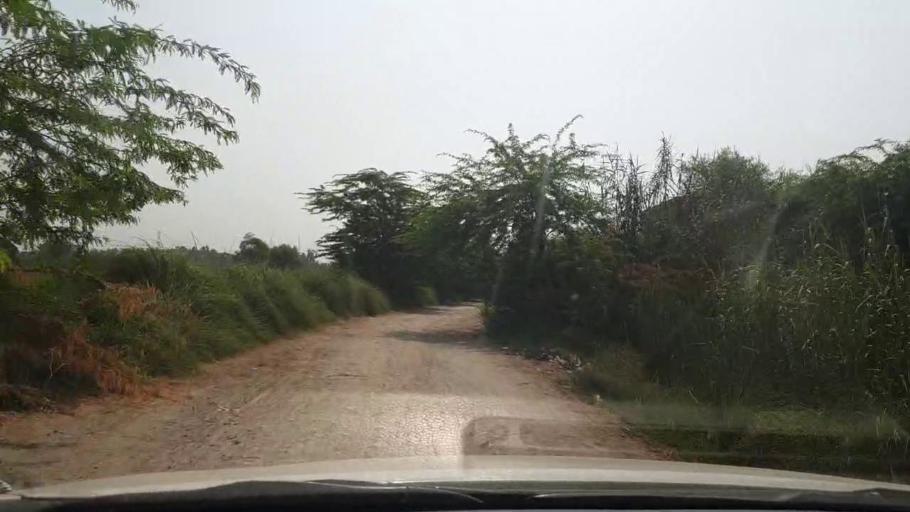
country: PK
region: Sindh
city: Shikarpur
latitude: 27.9756
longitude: 68.6756
